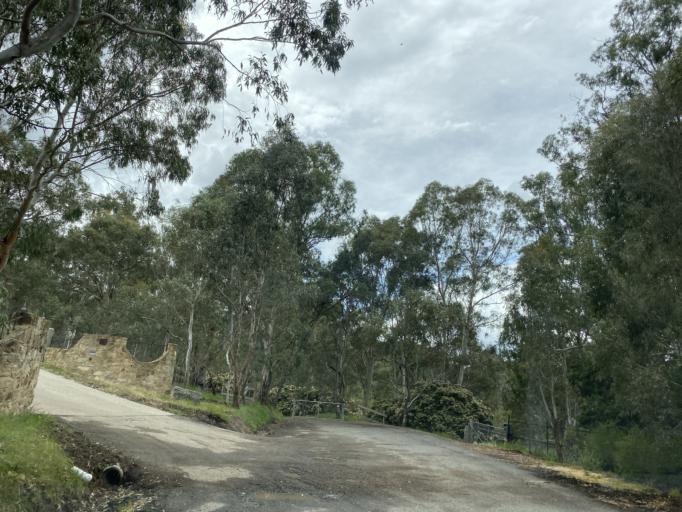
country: AU
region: Victoria
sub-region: Banyule
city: Darch
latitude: -37.7480
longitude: 145.1109
